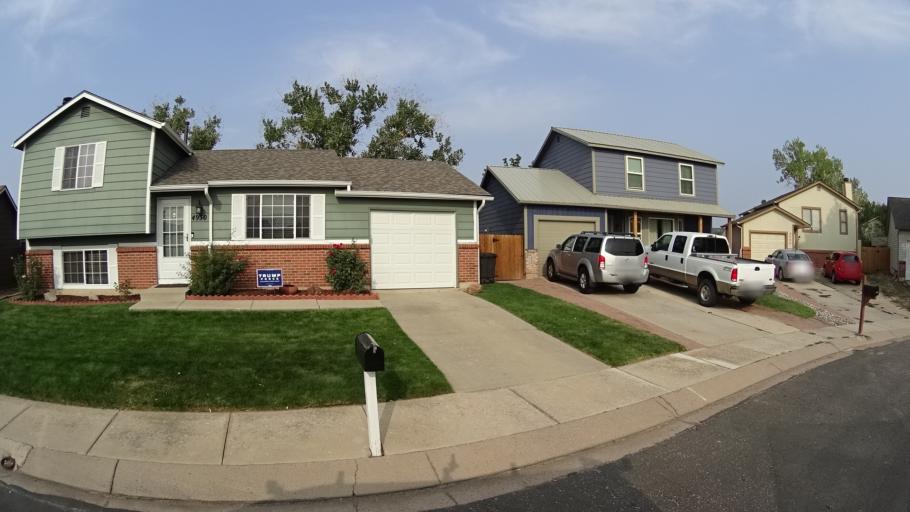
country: US
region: Colorado
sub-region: El Paso County
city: Stratmoor
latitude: 38.8014
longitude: -104.7352
